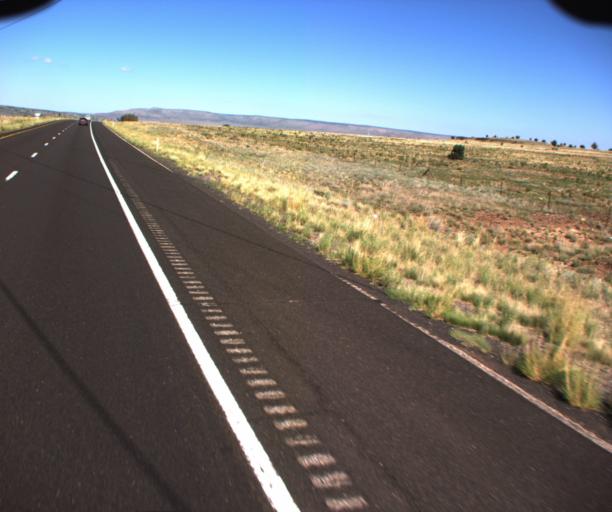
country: US
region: Arizona
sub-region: Yavapai County
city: Paulden
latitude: 35.2899
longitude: -112.8171
